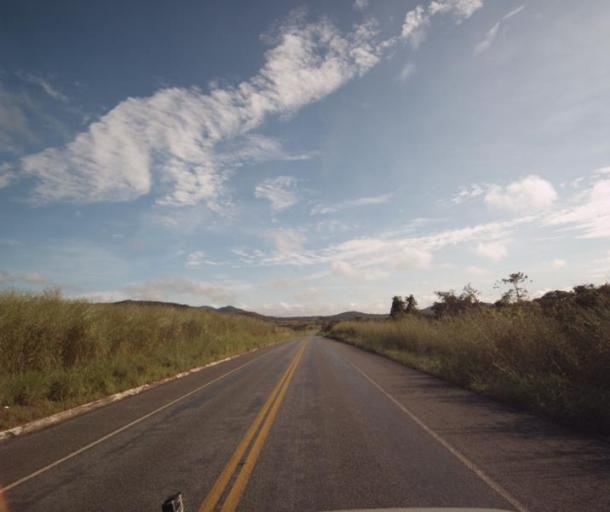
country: BR
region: Goias
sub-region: Pirenopolis
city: Pirenopolis
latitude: -15.5608
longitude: -48.6224
